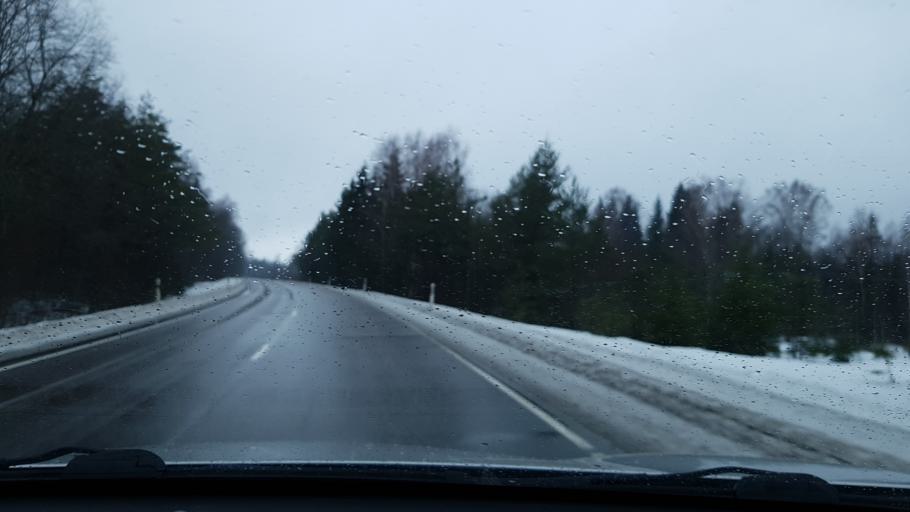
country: EE
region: Raplamaa
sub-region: Kehtna vald
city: Kehtna
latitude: 58.8828
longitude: 24.9764
